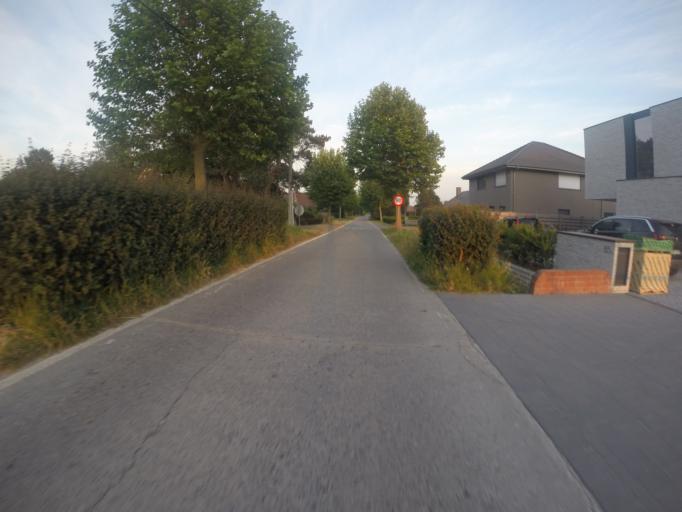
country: BE
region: Flanders
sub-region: Provincie Oost-Vlaanderen
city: Zomergem
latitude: 51.1202
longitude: 3.5360
